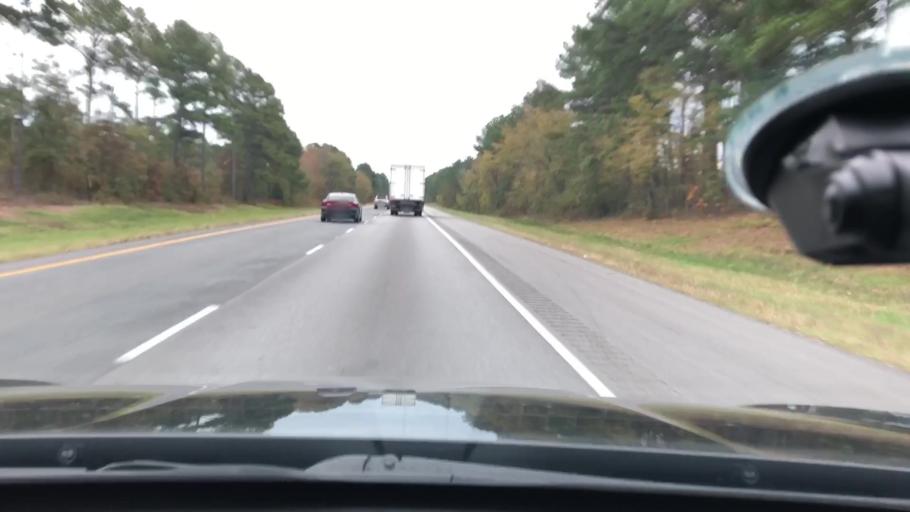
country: US
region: Arkansas
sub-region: Hempstead County
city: Hope
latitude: 33.6264
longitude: -93.7482
